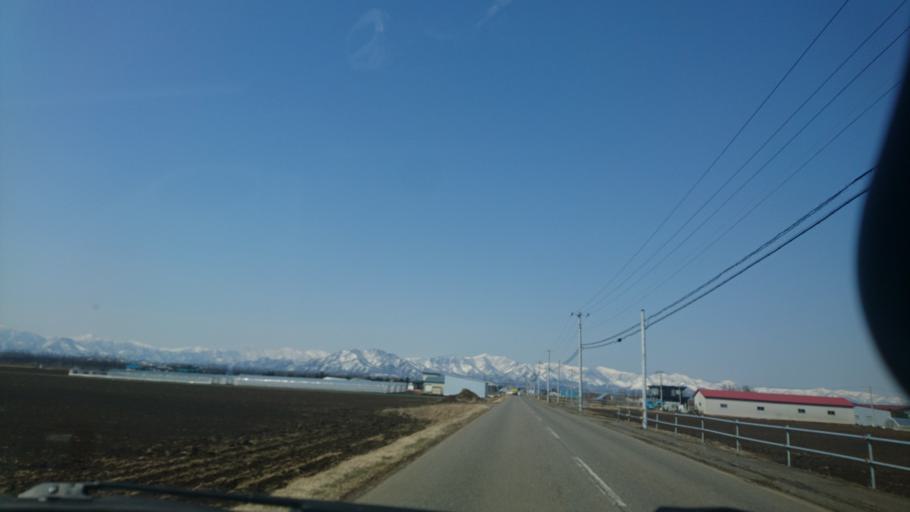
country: JP
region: Hokkaido
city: Obihiro
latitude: 42.9036
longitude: 143.0889
